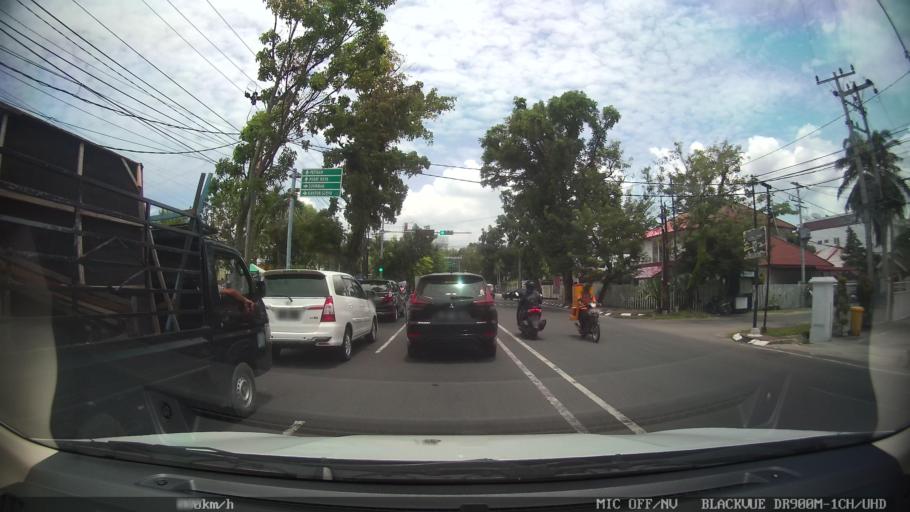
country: ID
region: North Sumatra
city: Medan
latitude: 3.5762
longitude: 98.6662
